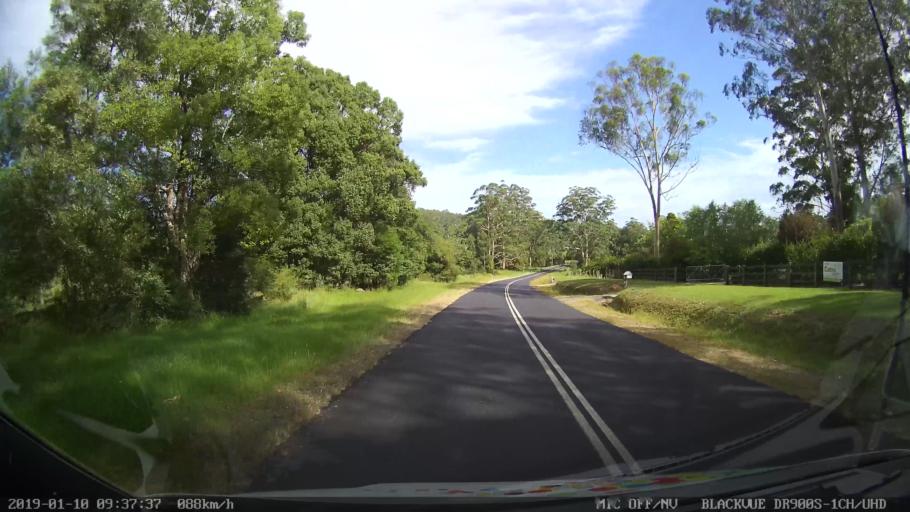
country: AU
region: New South Wales
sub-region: Coffs Harbour
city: Nana Glen
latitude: -30.1860
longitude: 153.0079
